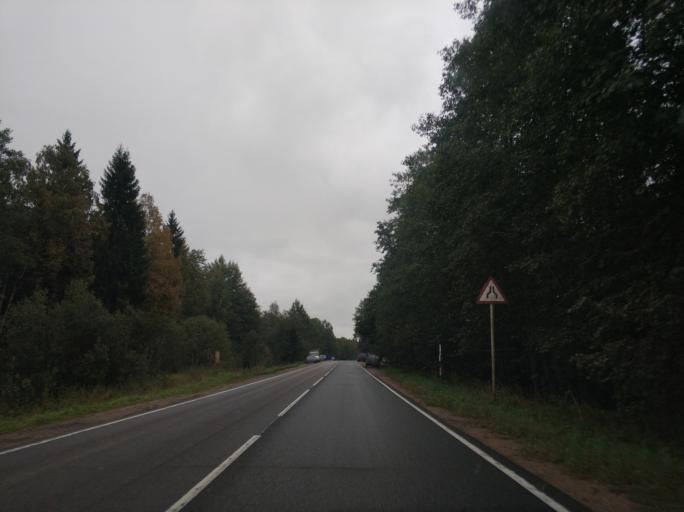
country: RU
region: Leningrad
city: Borisova Griva
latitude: 60.1364
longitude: 30.9578
